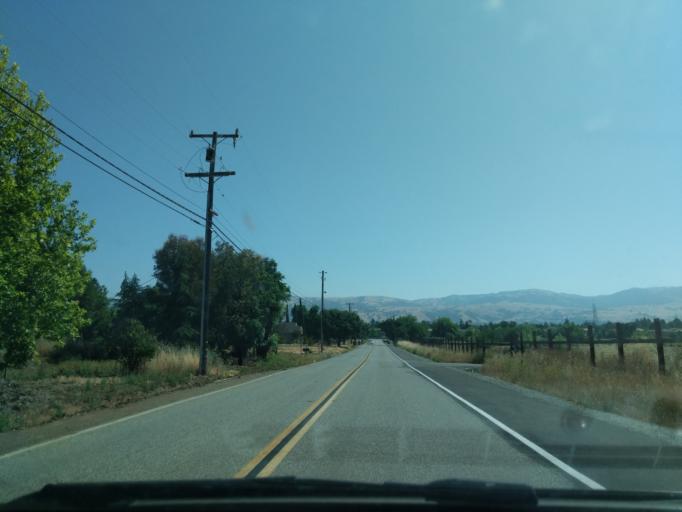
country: US
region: California
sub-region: Santa Clara County
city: Morgan Hill
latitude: 37.0948
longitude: -121.6517
